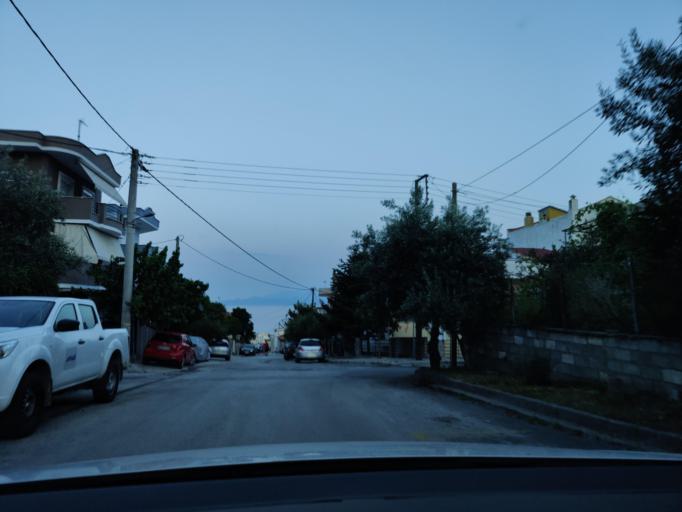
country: GR
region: East Macedonia and Thrace
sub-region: Nomos Kavalas
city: Kavala
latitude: 40.9267
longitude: 24.3831
